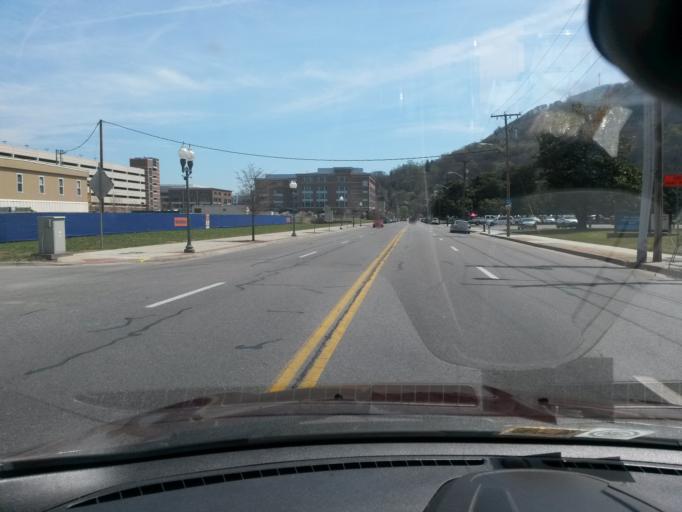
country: US
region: Virginia
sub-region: City of Roanoke
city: Cedar Bluff
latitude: 37.2558
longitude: -79.9465
